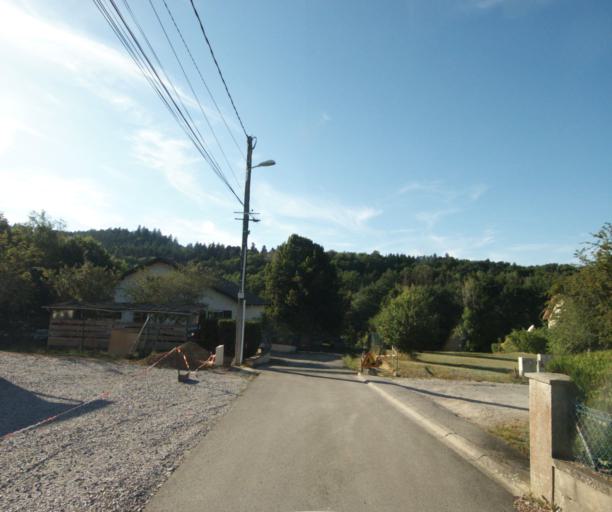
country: FR
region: Lorraine
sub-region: Departement des Vosges
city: Chantraine
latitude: 48.1473
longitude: 6.4441
